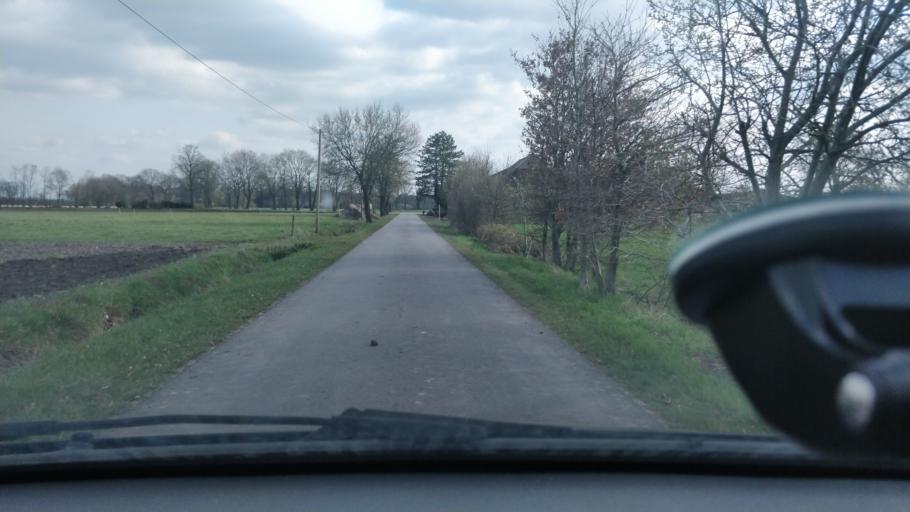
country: NL
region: Gelderland
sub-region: Gemeente Aalten
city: Bredevoort
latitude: 51.8910
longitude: 6.6302
